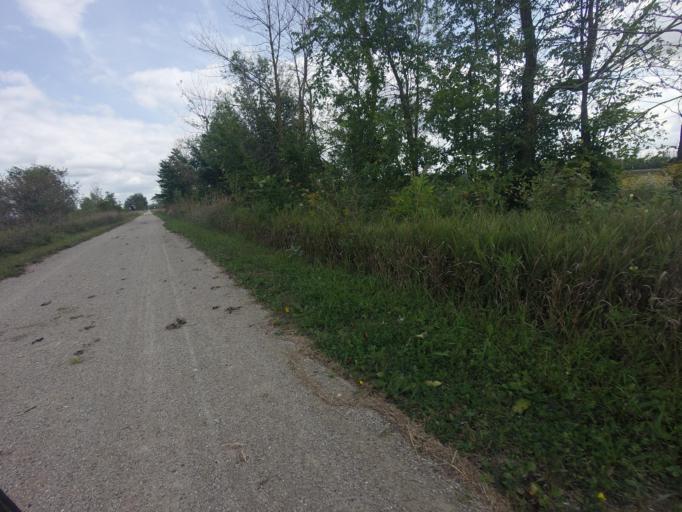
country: CA
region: Ontario
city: North Perth
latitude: 43.5719
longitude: -80.8669
